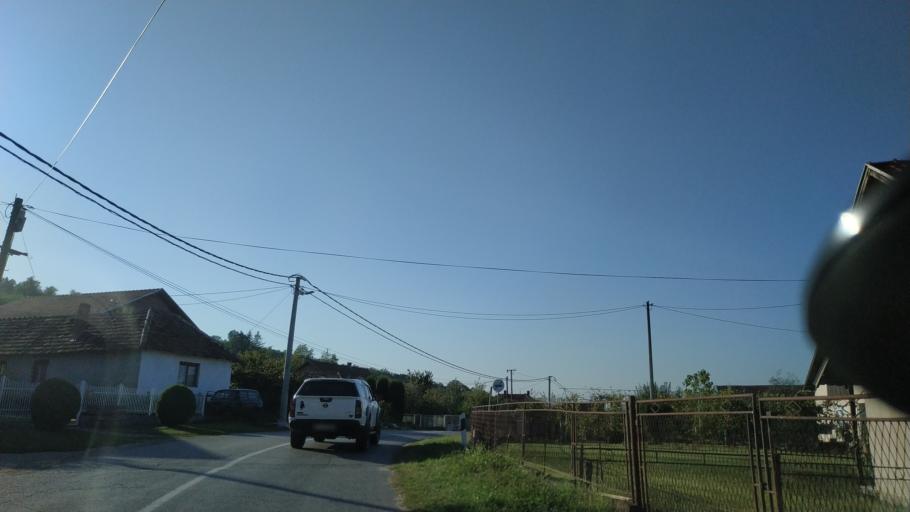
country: RS
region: Central Serbia
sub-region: Rasinski Okrug
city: Krusevac
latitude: 43.4835
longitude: 21.3500
